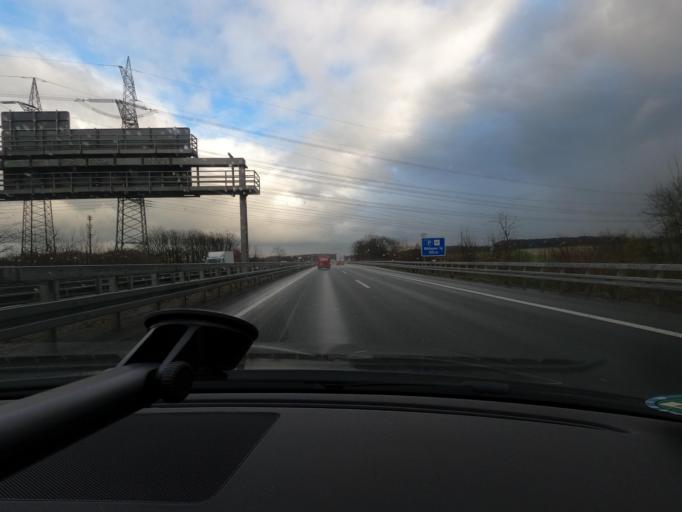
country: DE
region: North Rhine-Westphalia
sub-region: Regierungsbezirk Arnsberg
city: Unna
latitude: 51.5276
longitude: 7.7247
